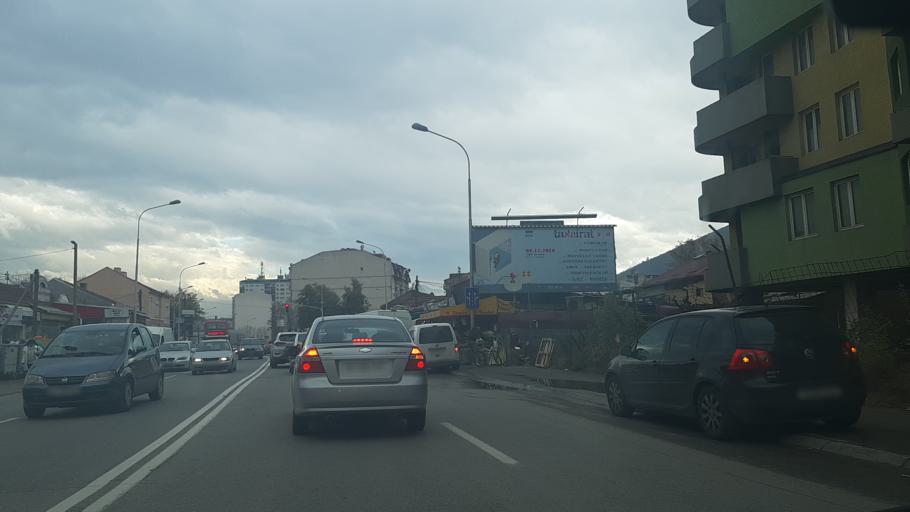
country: MK
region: Karpos
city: Skopje
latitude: 41.9846
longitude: 21.4384
